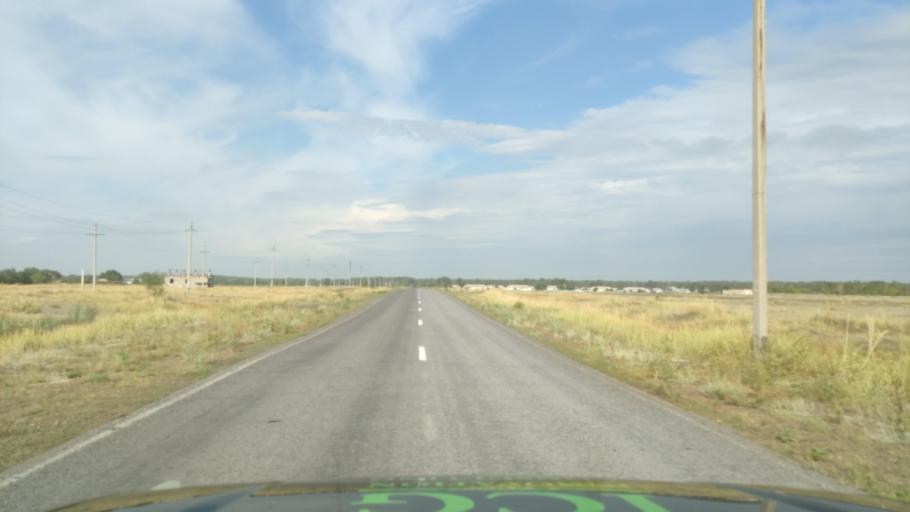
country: KZ
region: Pavlodar
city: Leninskiy
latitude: 52.4777
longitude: 76.8310
